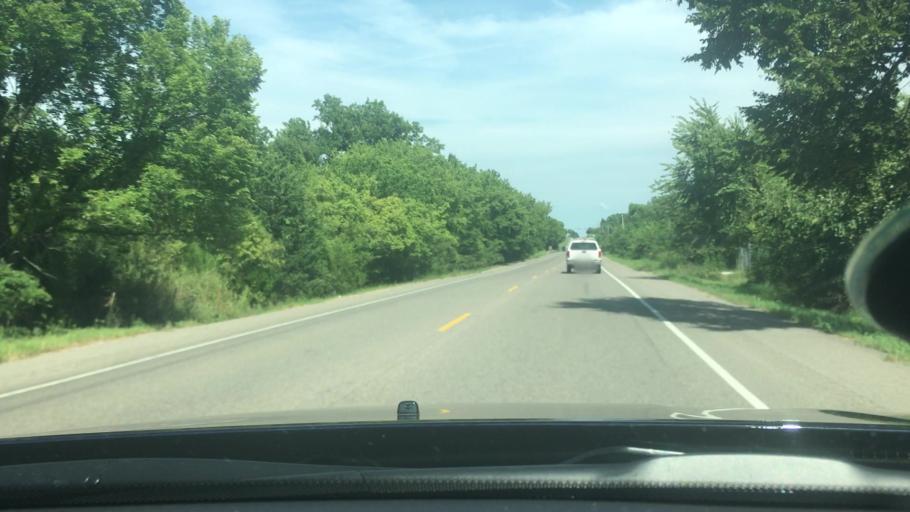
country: US
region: Oklahoma
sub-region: Pottawatomie County
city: Shawnee
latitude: 35.3330
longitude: -96.8150
